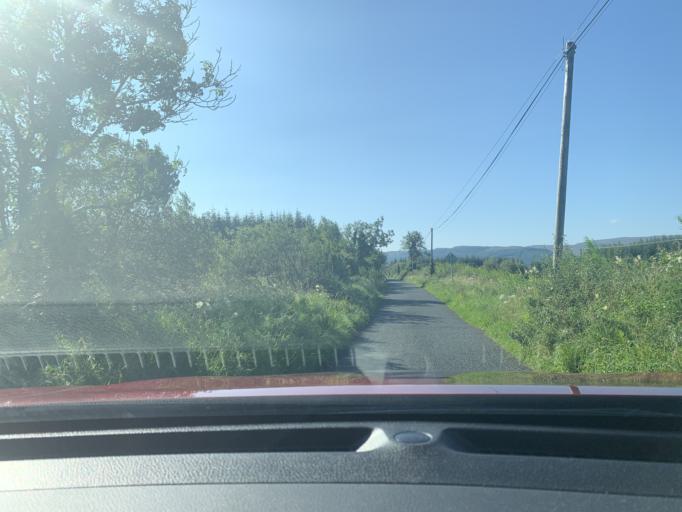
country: IE
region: Connaught
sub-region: Sligo
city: Tobercurry
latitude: 54.0725
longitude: -8.7763
